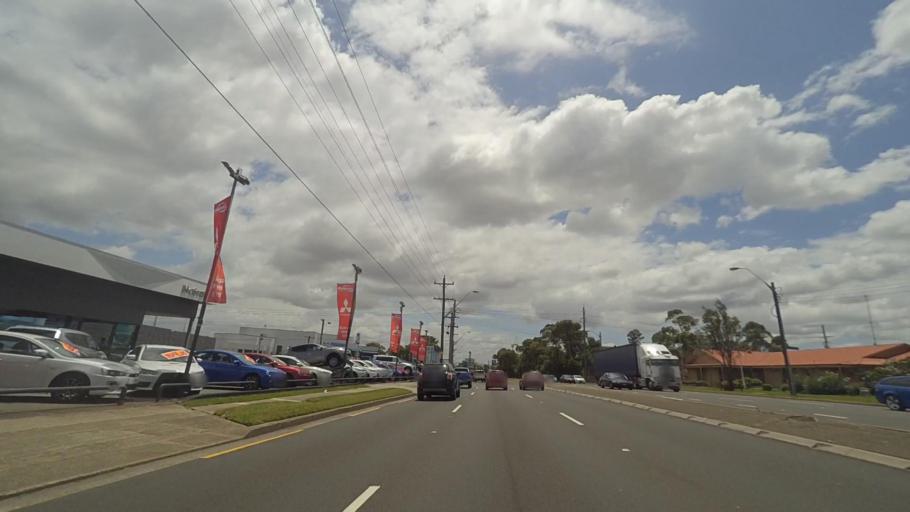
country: AU
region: New South Wales
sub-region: Liverpool
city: Miller
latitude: -33.9341
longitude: 150.9160
